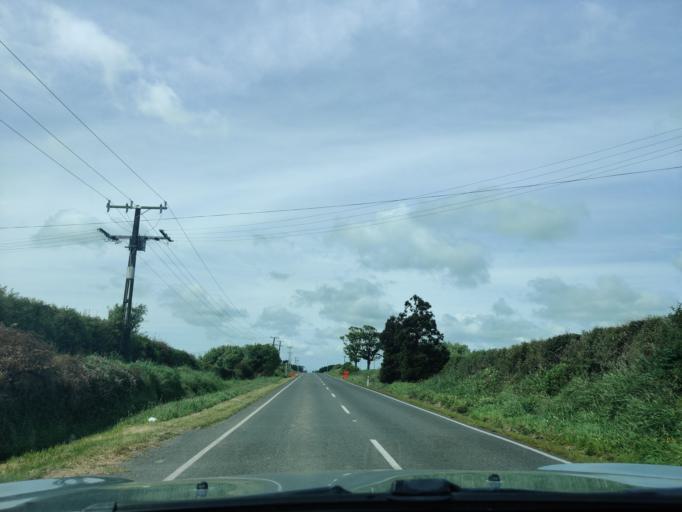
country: NZ
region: Taranaki
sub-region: South Taranaki District
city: Eltham
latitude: -39.4277
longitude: 174.1664
